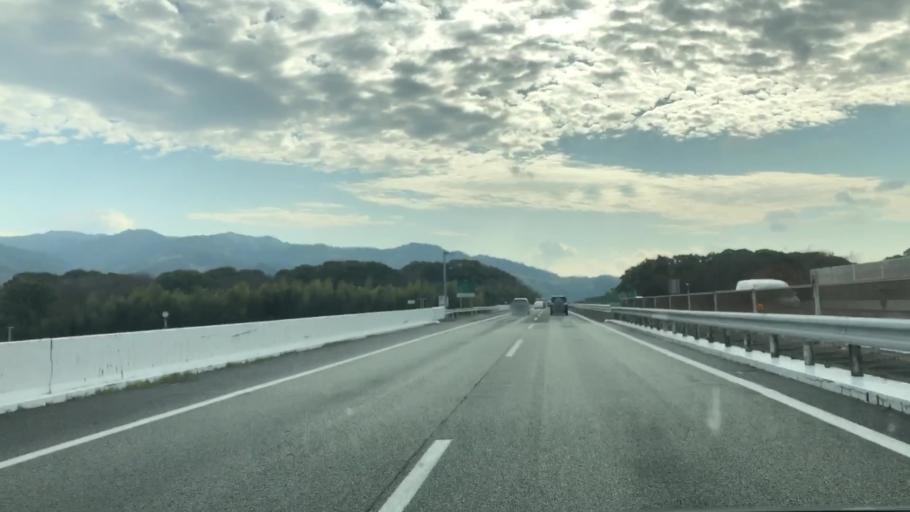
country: JP
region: Fukuoka
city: Setakamachi-takayanagi
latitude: 33.1844
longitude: 130.5187
